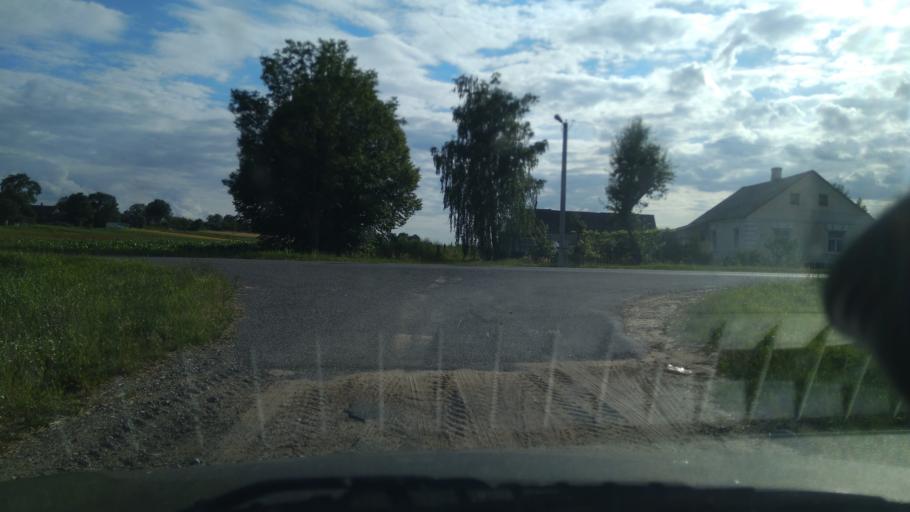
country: BY
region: Grodnenskaya
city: Masty
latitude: 53.3135
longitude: 24.6944
